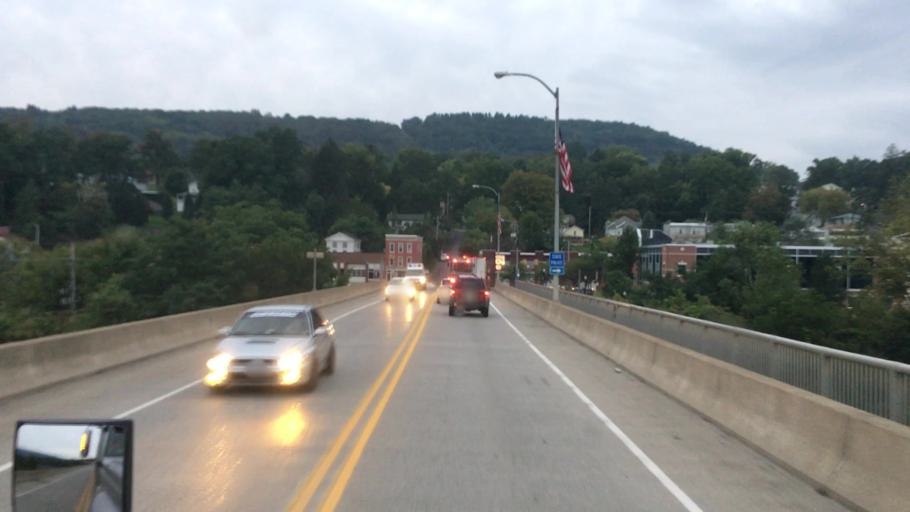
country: US
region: Pennsylvania
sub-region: Bradford County
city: Towanda
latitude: 41.7623
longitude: -76.4408
